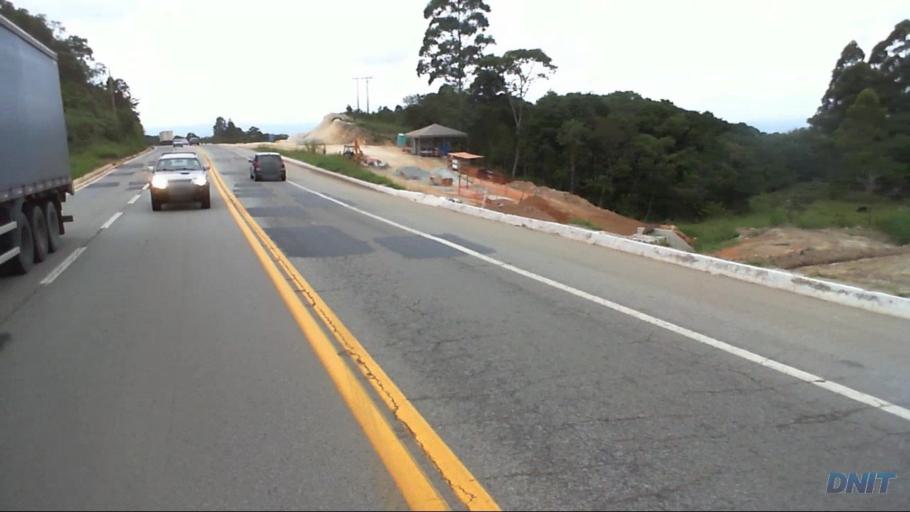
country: BR
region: Minas Gerais
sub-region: Caete
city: Caete
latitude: -19.7530
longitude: -43.5272
